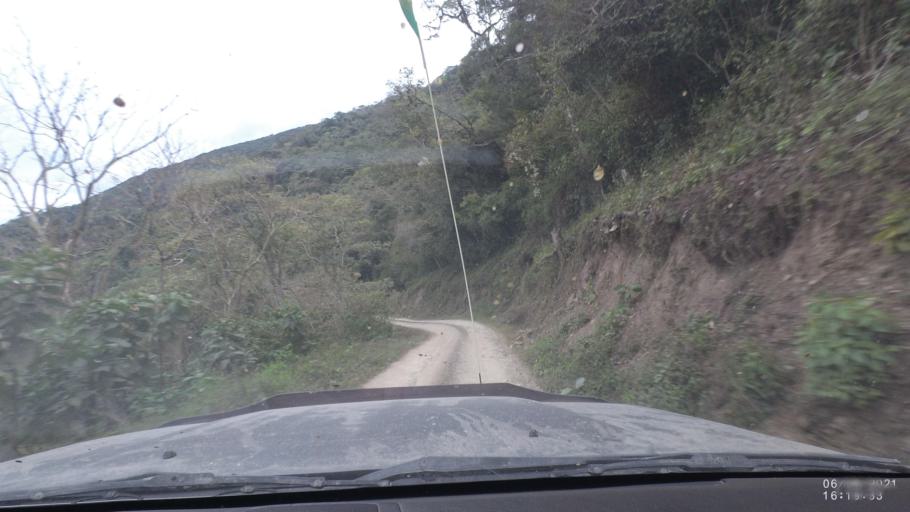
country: BO
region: La Paz
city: Quime
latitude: -16.5495
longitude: -66.7450
